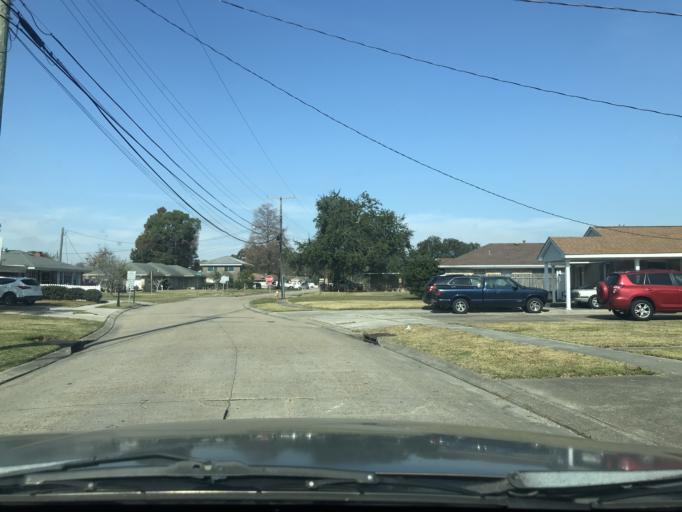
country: US
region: Louisiana
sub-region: Jefferson Parish
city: Marrero
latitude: 29.8921
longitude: -90.0891
